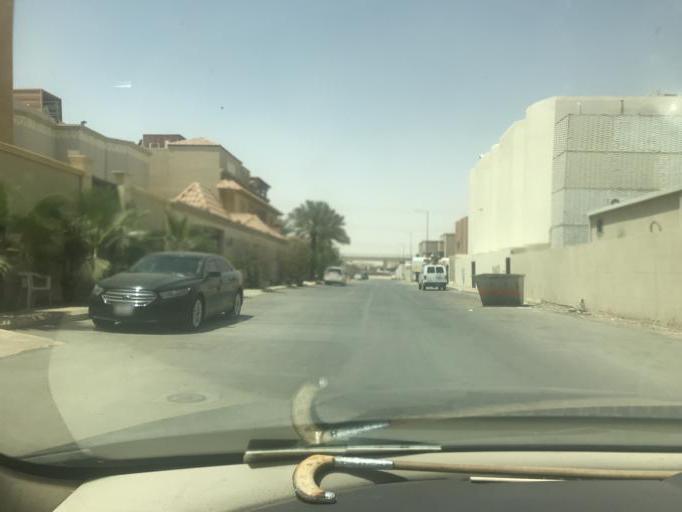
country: SA
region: Ar Riyad
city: Riyadh
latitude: 24.7979
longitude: 46.6967
